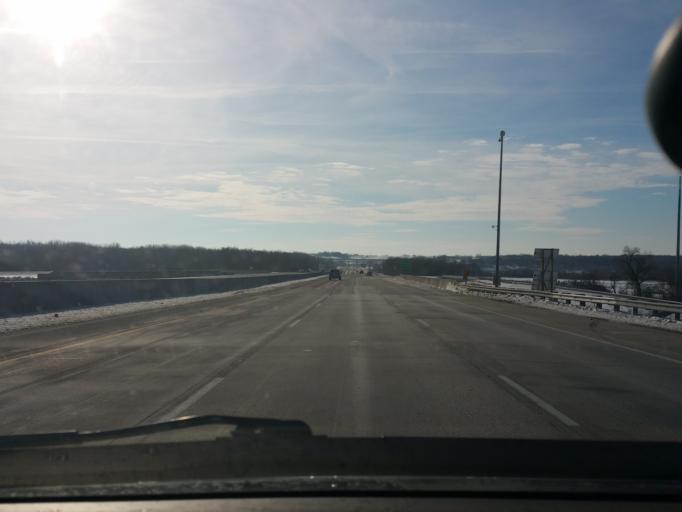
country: US
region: Iowa
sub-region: Polk County
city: West Des Moines
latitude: 41.5424
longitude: -93.7756
